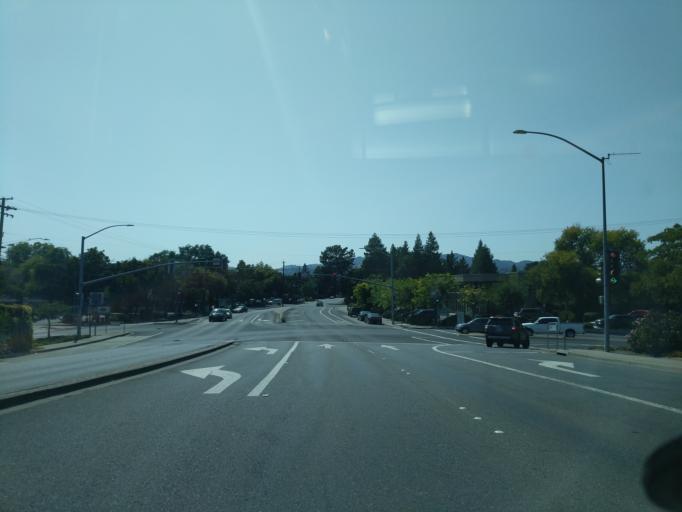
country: US
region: California
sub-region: Contra Costa County
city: Waldon
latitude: 37.9336
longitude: -122.0617
